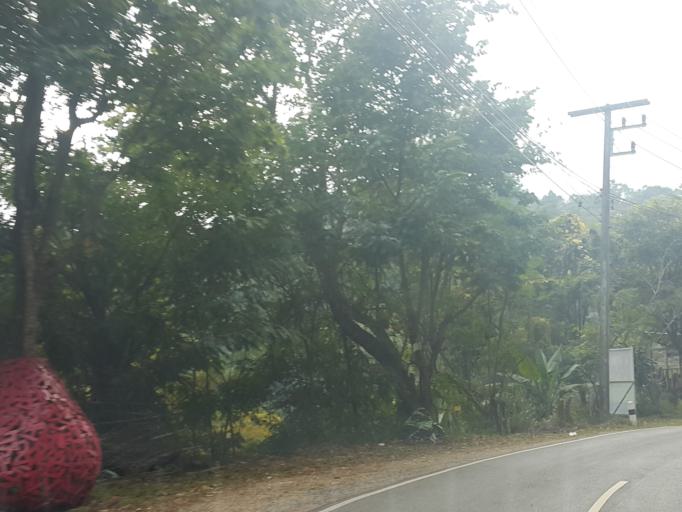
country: TH
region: Chiang Mai
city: Samoeng
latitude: 18.9140
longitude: 98.8234
